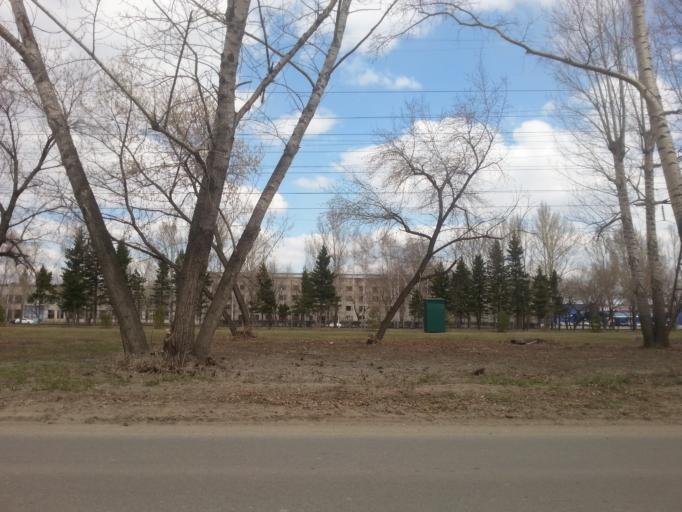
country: RU
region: Altai Krai
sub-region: Gorod Barnaulskiy
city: Barnaul
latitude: 53.3859
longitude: 83.7270
